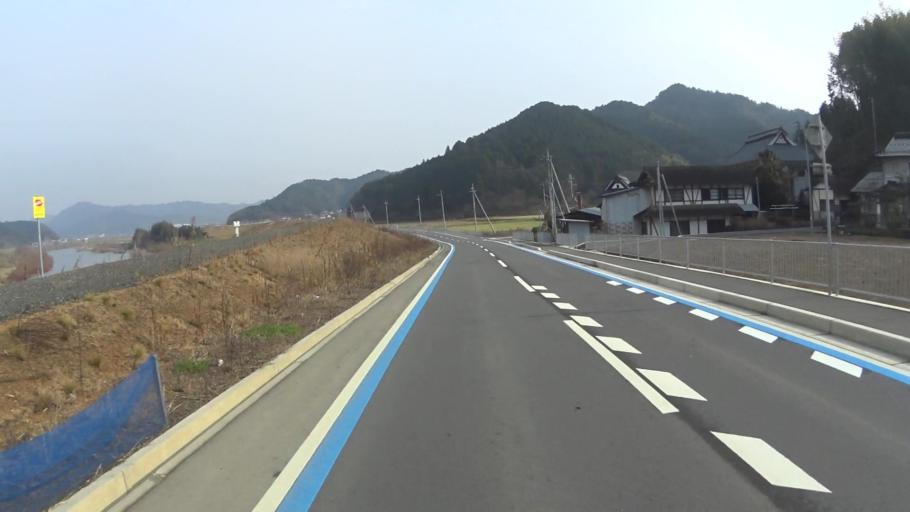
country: JP
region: Kyoto
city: Fukuchiyama
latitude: 35.3707
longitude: 135.1341
